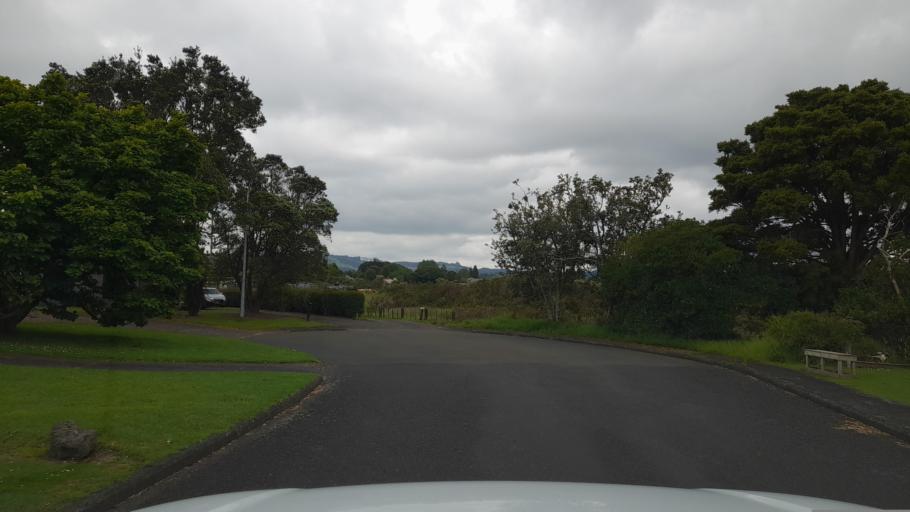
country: NZ
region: Northland
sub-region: Far North District
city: Waimate North
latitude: -35.4049
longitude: 173.7900
